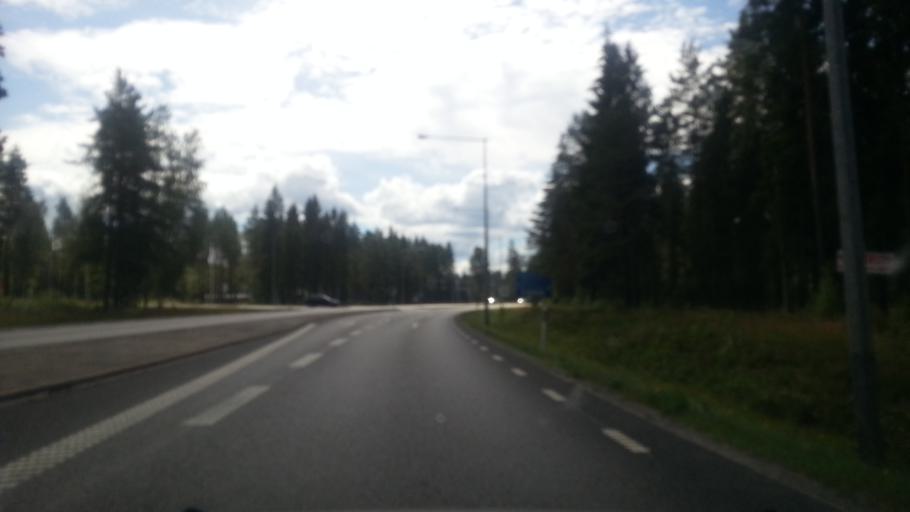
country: SE
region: OErebro
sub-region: Lindesbergs Kommun
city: Lindesberg
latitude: 59.6186
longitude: 15.1893
